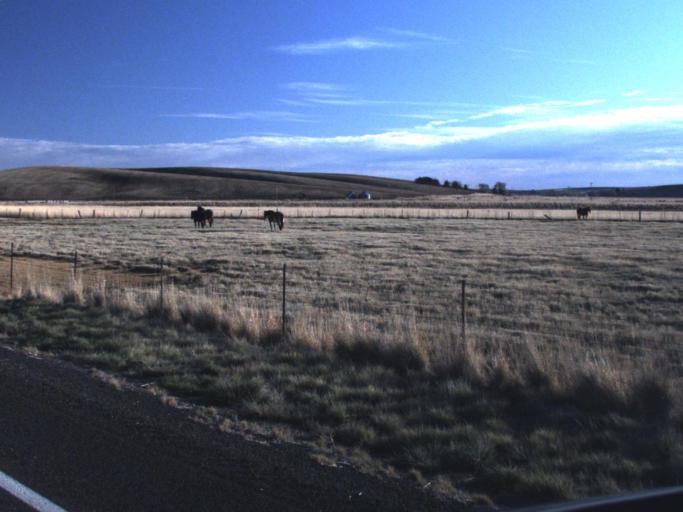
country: US
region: Washington
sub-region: Garfield County
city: Pomeroy
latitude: 46.7721
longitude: -117.7059
